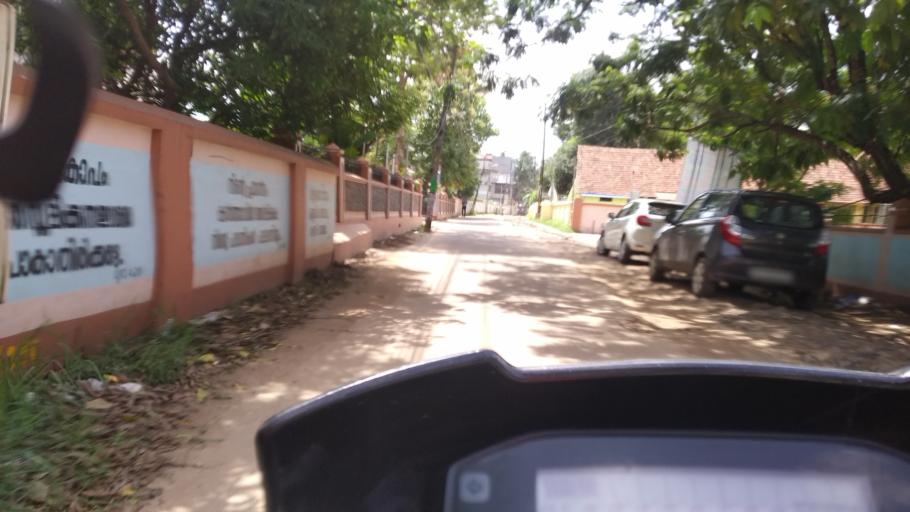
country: IN
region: Kerala
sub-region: Ernakulam
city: Cochin
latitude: 9.9856
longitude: 76.2949
